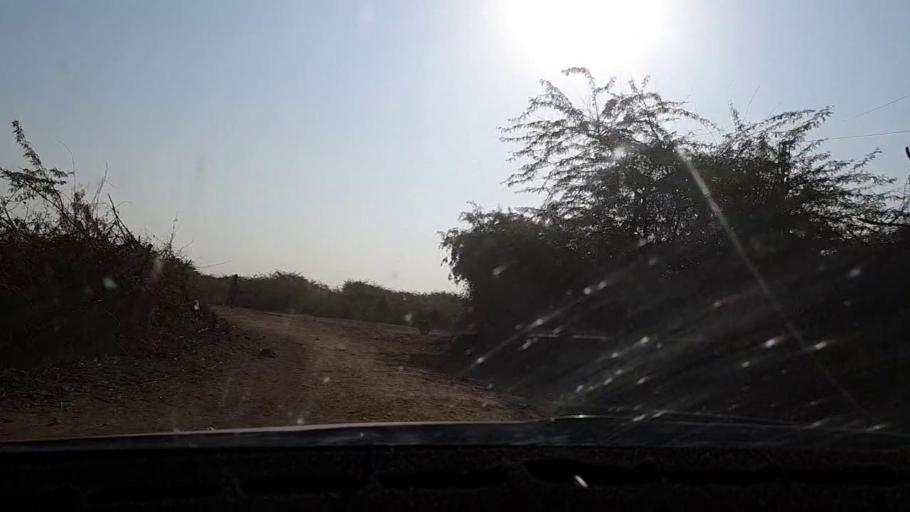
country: PK
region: Sindh
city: Tando Mittha Khan
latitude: 25.8355
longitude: 69.3176
